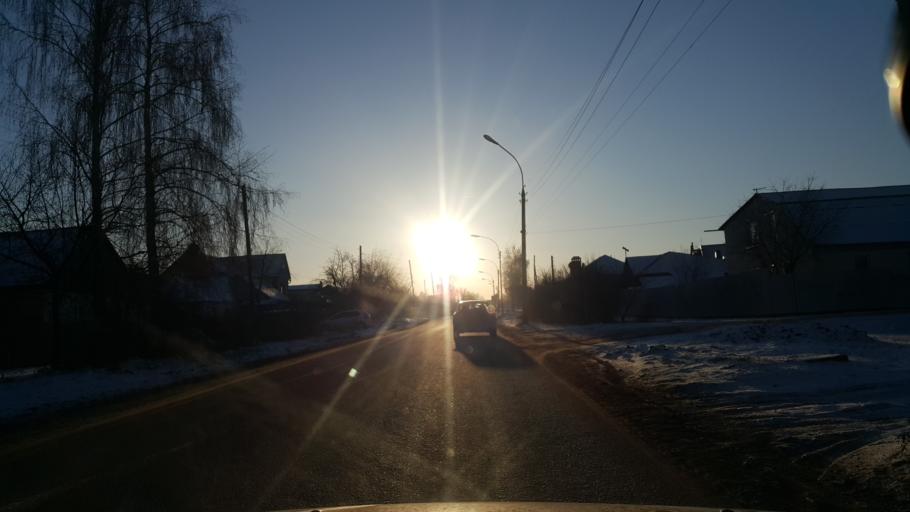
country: RU
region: Tambov
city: Pokrovo-Prigorodnoye
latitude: 52.7025
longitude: 41.4069
